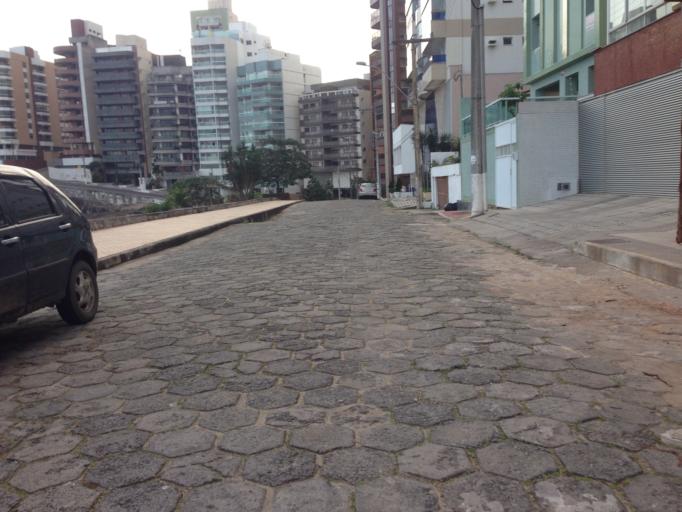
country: BR
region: Espirito Santo
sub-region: Guarapari
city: Guarapari
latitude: -20.6692
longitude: -40.4924
